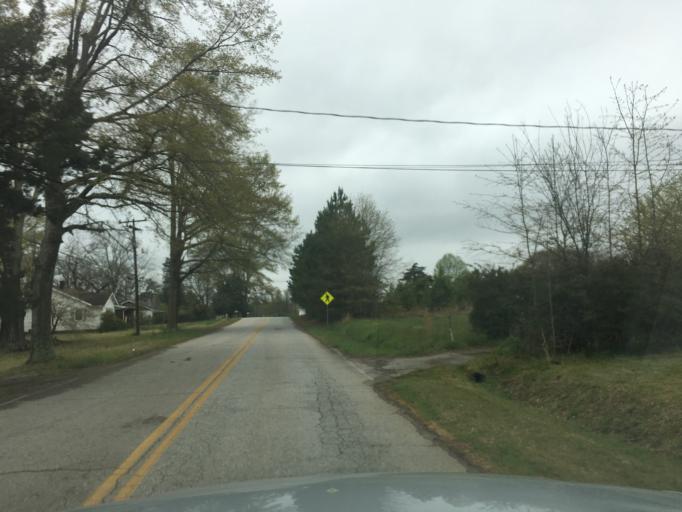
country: US
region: South Carolina
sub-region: Spartanburg County
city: Southern Shops
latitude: 34.9804
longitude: -82.0004
